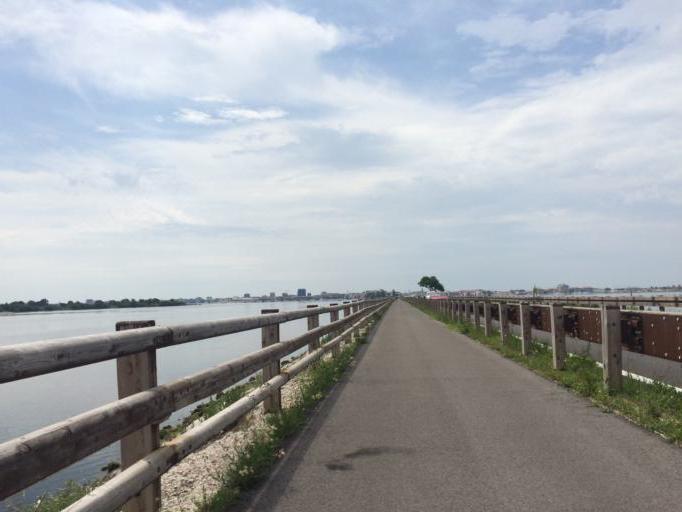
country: IT
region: Friuli Venezia Giulia
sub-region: Provincia di Gorizia
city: Grado
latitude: 45.6988
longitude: 13.3835
